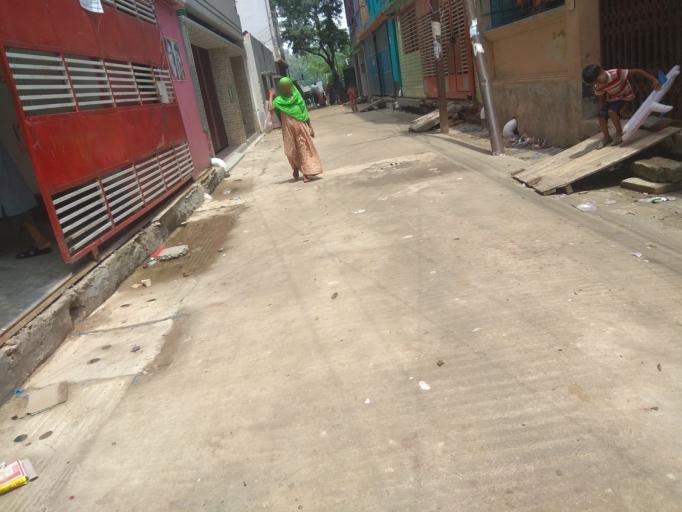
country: BD
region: Dhaka
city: Tungi
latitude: 23.8176
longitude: 90.3535
